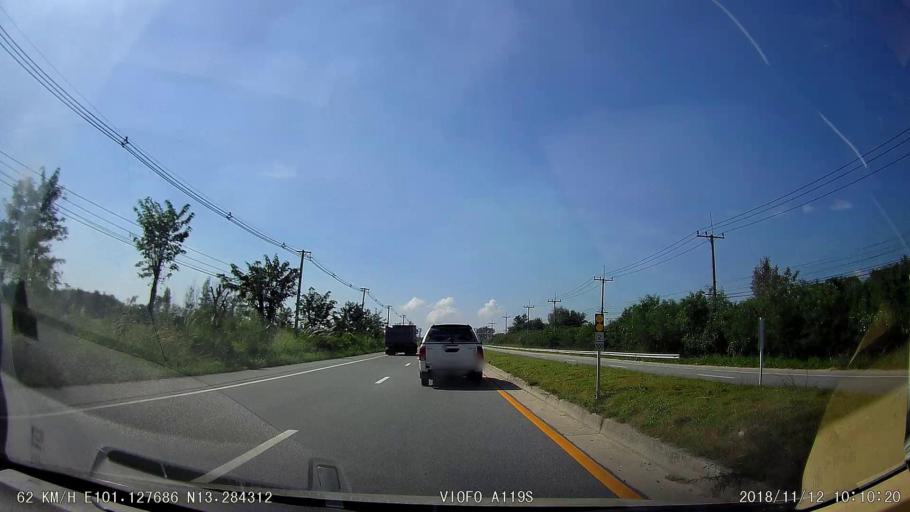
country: TH
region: Chon Buri
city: Ban Bueng
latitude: 13.2841
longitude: 101.1278
